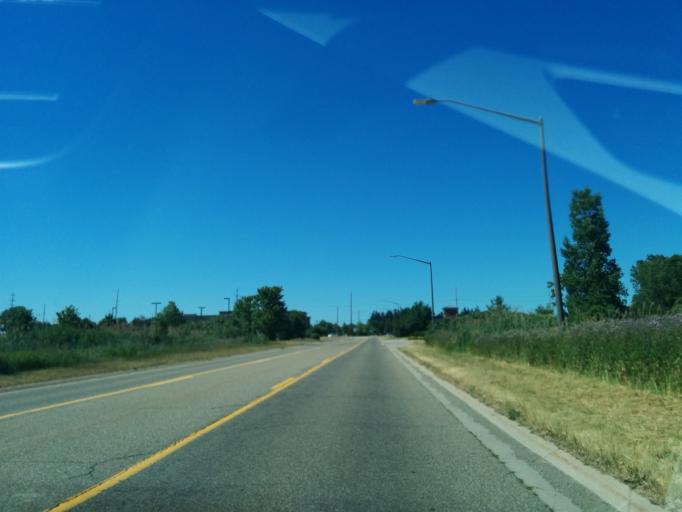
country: US
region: Michigan
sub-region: Oakland County
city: Wolverine Lake
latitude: 42.5390
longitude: -83.4501
